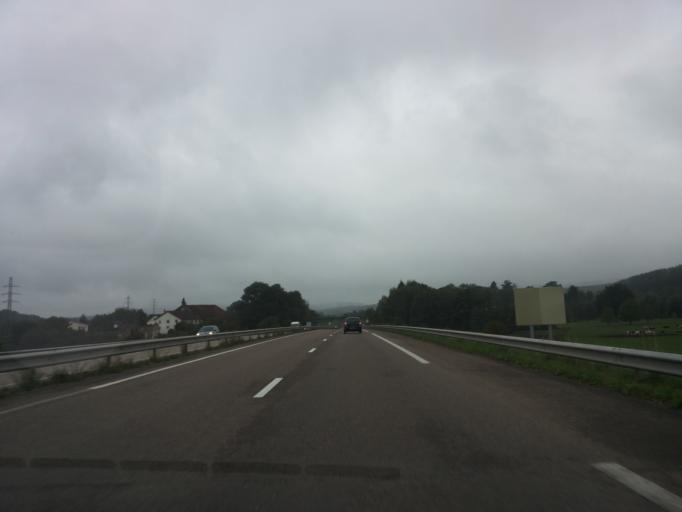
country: FR
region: Lorraine
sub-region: Departement des Vosges
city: Pouxeux
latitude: 48.1120
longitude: 6.5642
